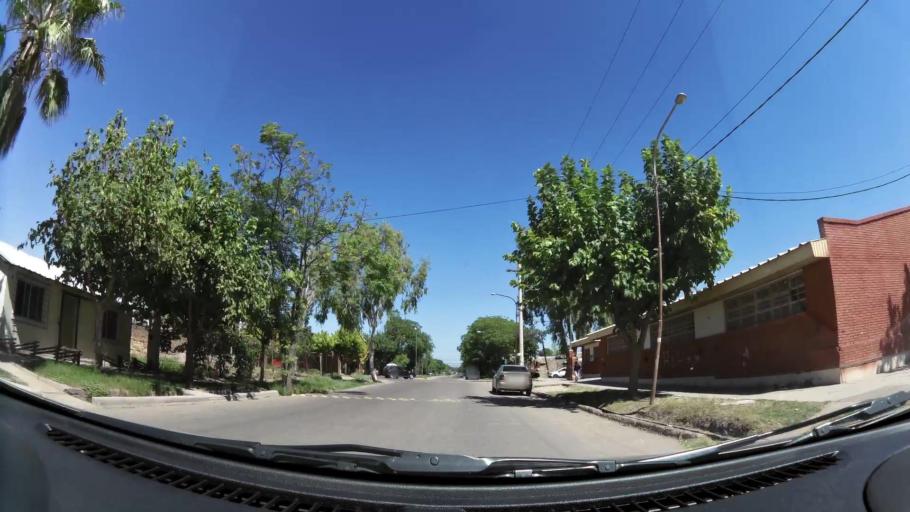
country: AR
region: Mendoza
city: Villa Nueva
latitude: -32.8802
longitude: -68.7878
